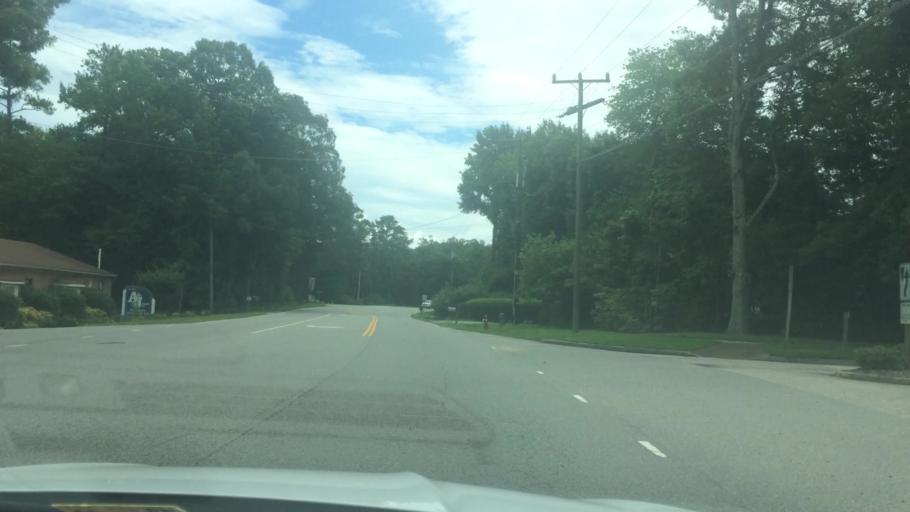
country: US
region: Virginia
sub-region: James City County
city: Williamsburg
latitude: 37.2501
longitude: -76.7647
